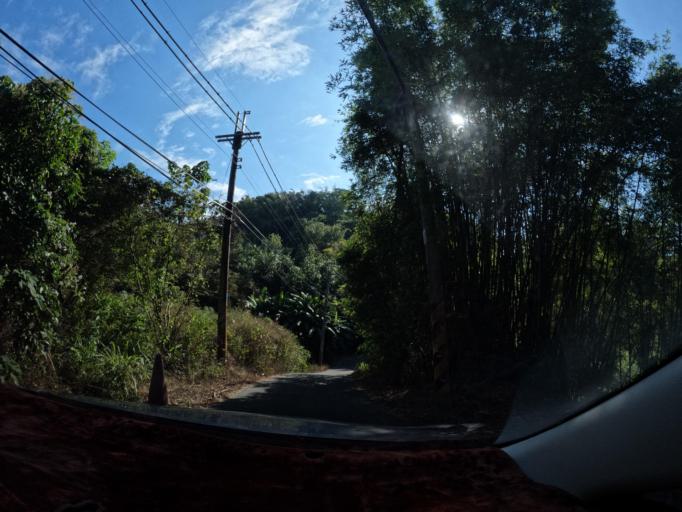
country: TW
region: Taiwan
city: Yujing
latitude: 23.0267
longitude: 120.3923
